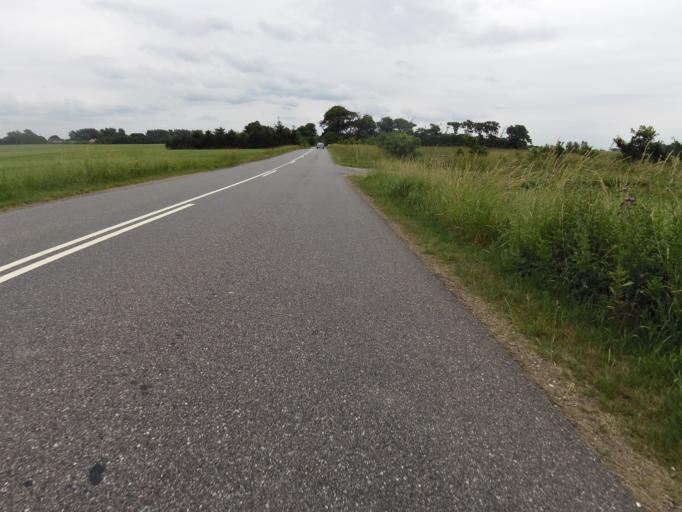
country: DK
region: Central Jutland
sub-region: Holstebro Kommune
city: Vinderup
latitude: 56.4121
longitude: 8.7079
